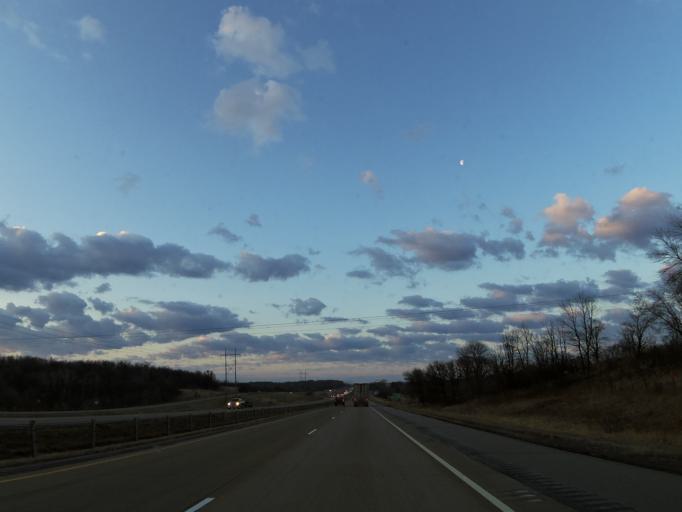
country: US
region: Minnesota
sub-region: Scott County
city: Elko New Market
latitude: 44.4869
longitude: -93.2920
